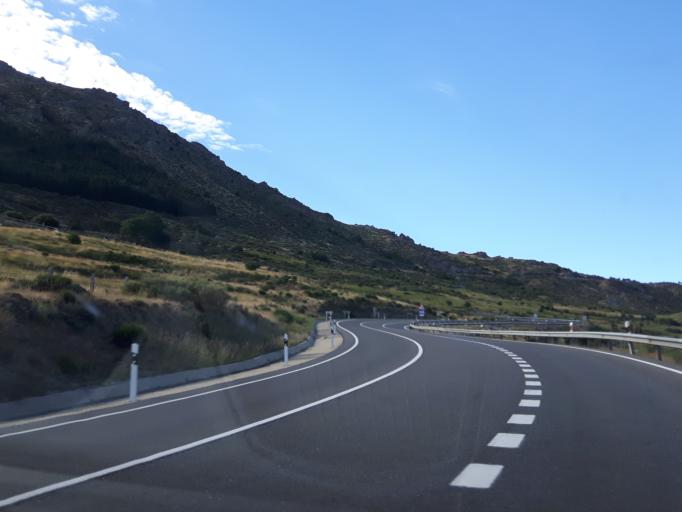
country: ES
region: Castille and Leon
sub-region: Provincia de Avila
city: Mengamunoz
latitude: 40.4882
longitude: -5.0094
